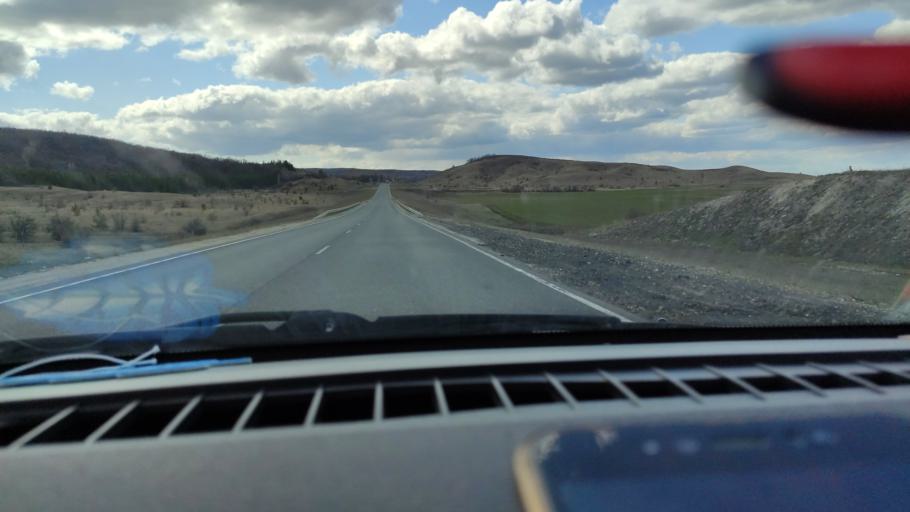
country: RU
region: Saratov
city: Alekseyevka
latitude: 52.3759
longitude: 47.9715
